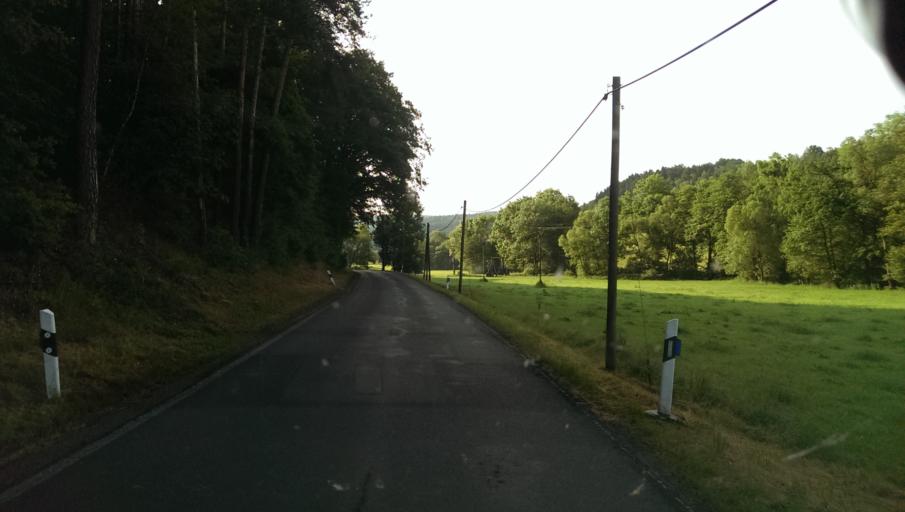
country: DE
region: Thuringia
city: Rottenbach
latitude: 50.7034
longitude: 11.1995
